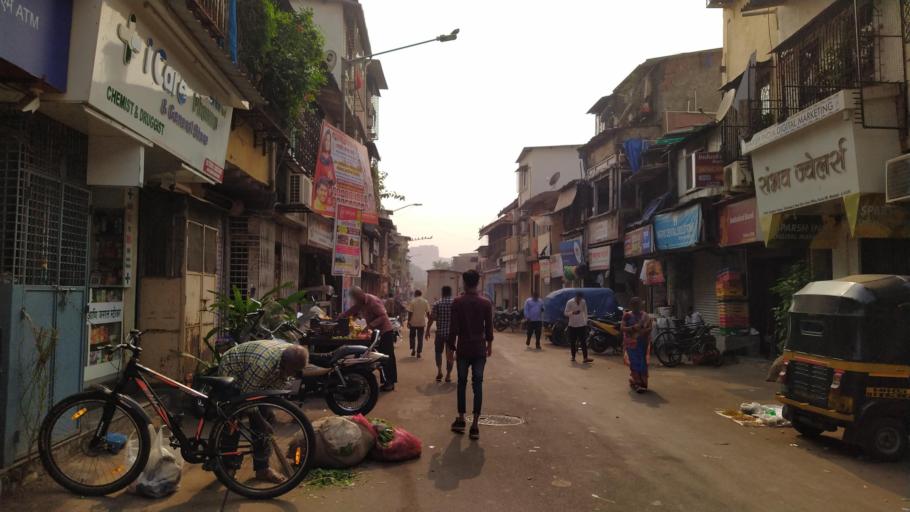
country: IN
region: Maharashtra
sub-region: Mumbai Suburban
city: Mumbai
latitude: 19.0635
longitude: 72.8752
